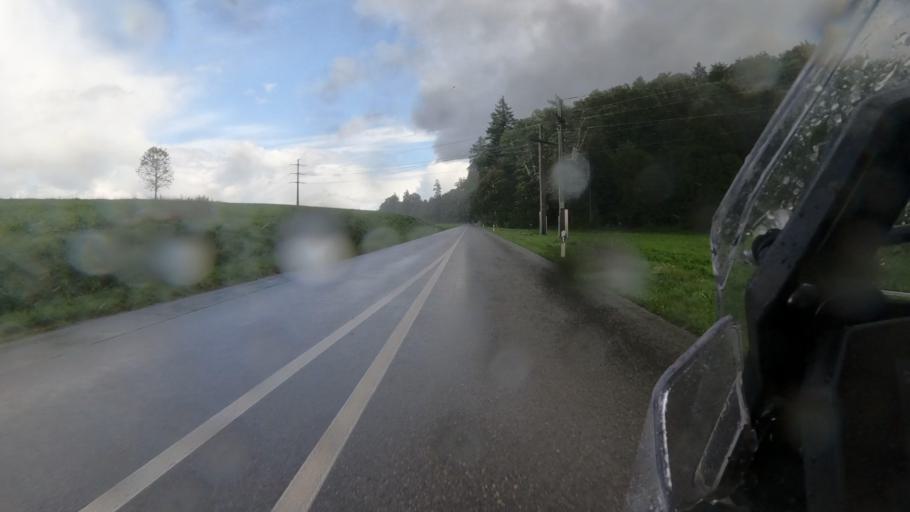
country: CH
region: Zurich
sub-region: Bezirk Andelfingen
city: Marthalen
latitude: 47.6402
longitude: 8.6312
